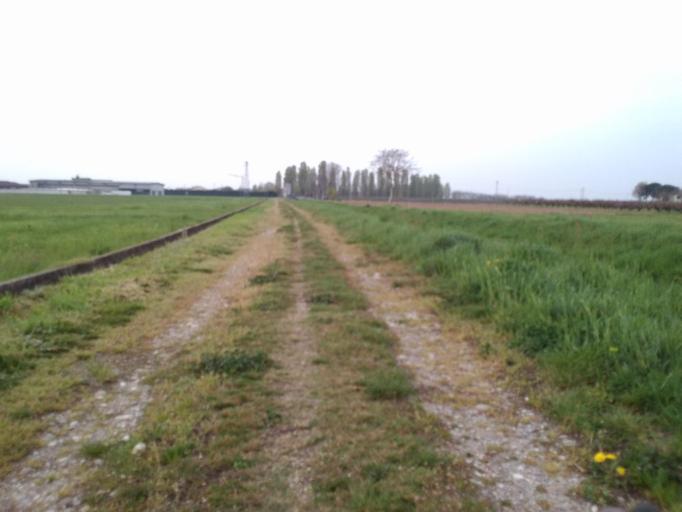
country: IT
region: Veneto
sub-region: Provincia di Verona
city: Villafranca di Verona
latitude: 45.3325
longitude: 10.8550
